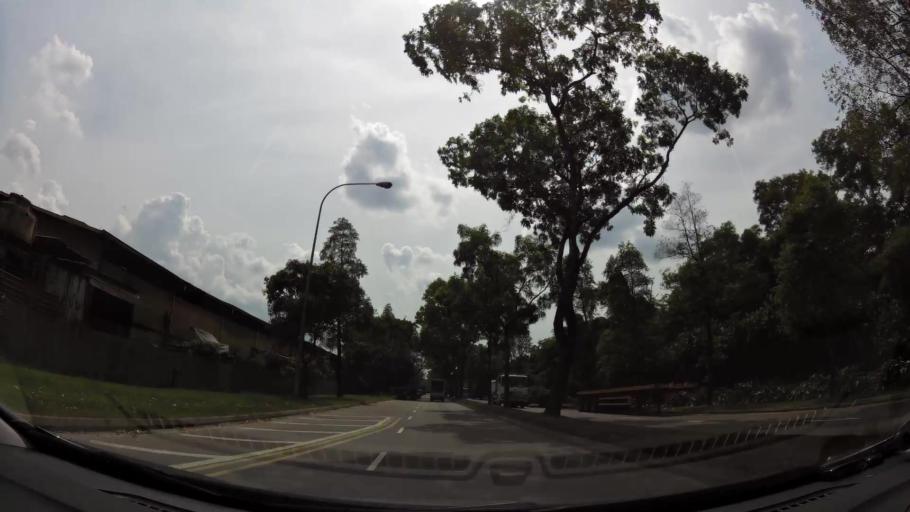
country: MY
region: Johor
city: Johor Bahru
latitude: 1.4266
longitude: 103.7469
